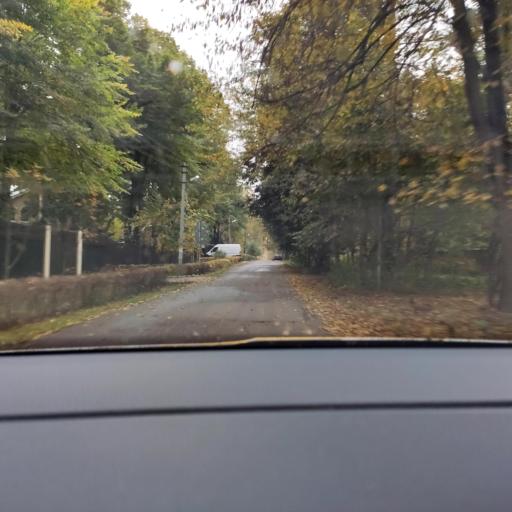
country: RU
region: Moskovskaya
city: Mamontovka
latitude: 55.9812
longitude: 37.8349
